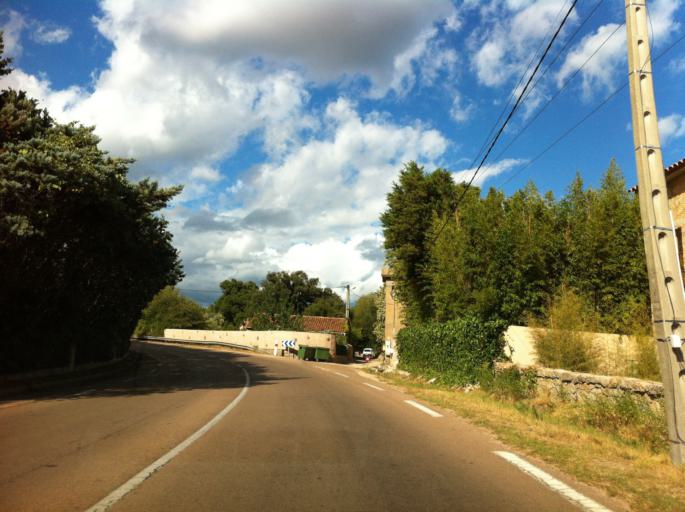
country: FR
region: Corsica
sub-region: Departement de la Corse-du-Sud
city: Porto-Vecchio
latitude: 41.6310
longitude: 9.2912
